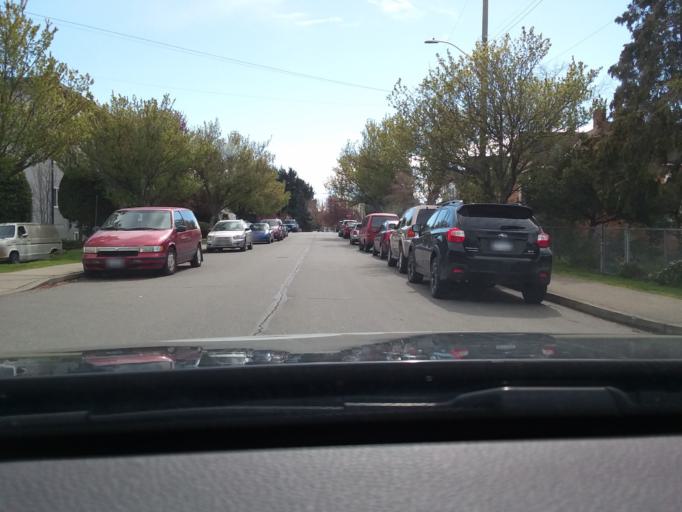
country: CA
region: British Columbia
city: Victoria
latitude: 48.4325
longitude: -123.3474
